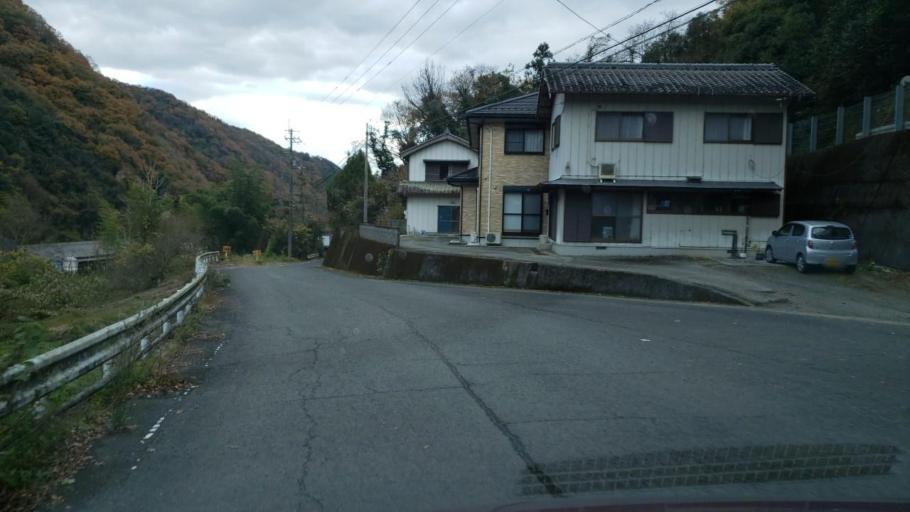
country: JP
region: Tokushima
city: Wakimachi
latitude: 34.1236
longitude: 134.2260
